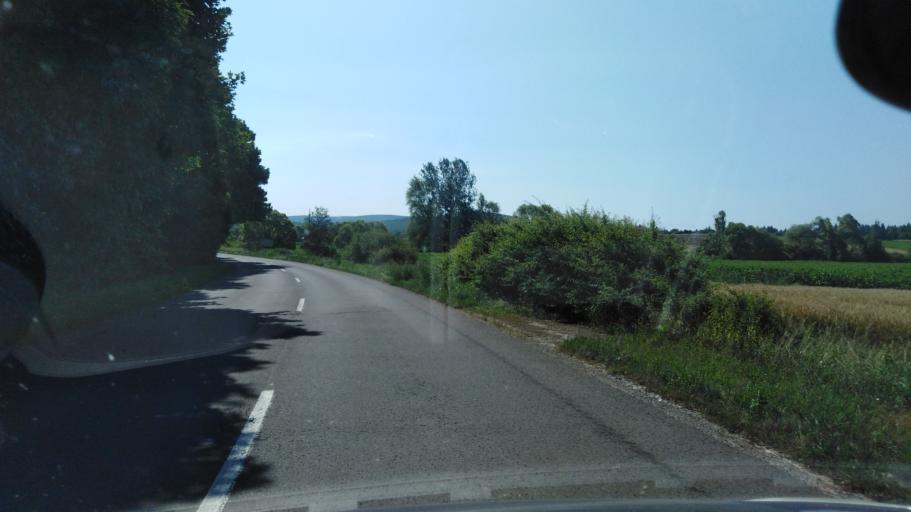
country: HU
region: Nograd
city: Retsag
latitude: 47.9314
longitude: 19.1645
